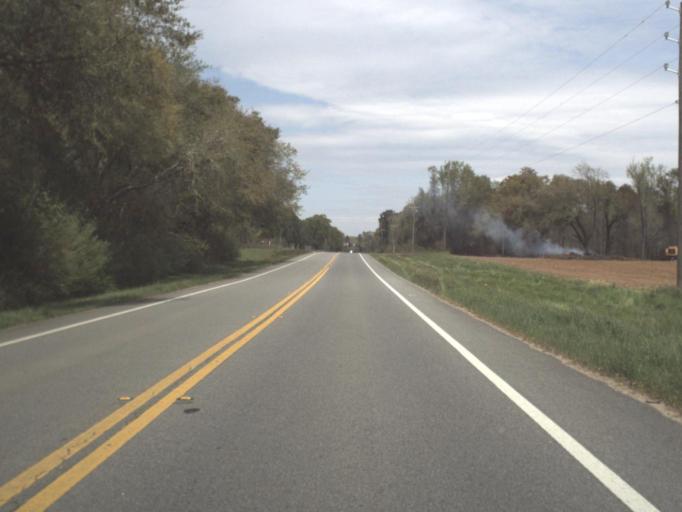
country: US
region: Florida
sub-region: Jackson County
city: Graceville
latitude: 30.9150
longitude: -85.4303
